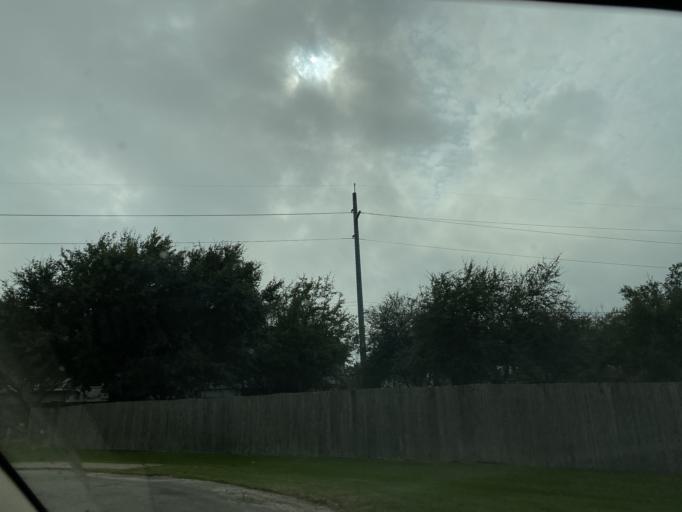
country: US
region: Texas
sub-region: Harris County
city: Hunters Creek Village
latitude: 29.7364
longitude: -95.4828
